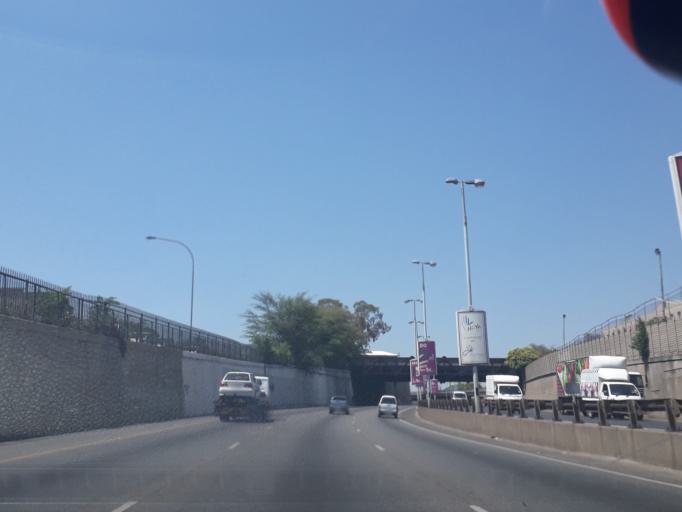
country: ZA
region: Gauteng
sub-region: City of Johannesburg Metropolitan Municipality
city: Johannesburg
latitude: -26.1898
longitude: 28.0279
